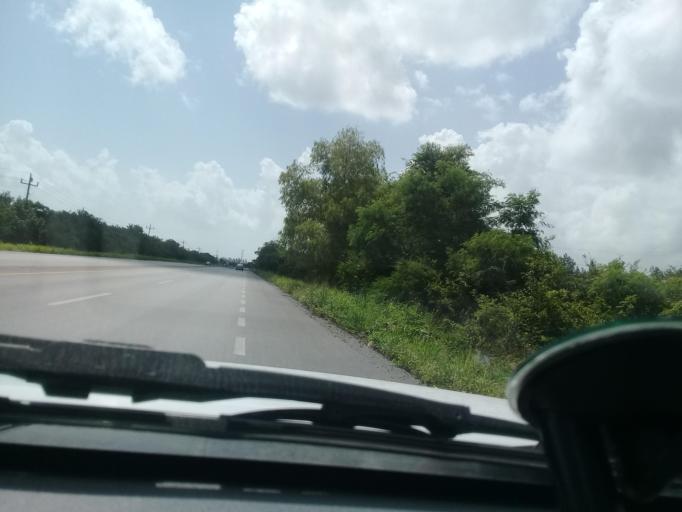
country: MX
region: Veracruz
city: Moralillo
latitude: 22.2127
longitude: -97.9692
